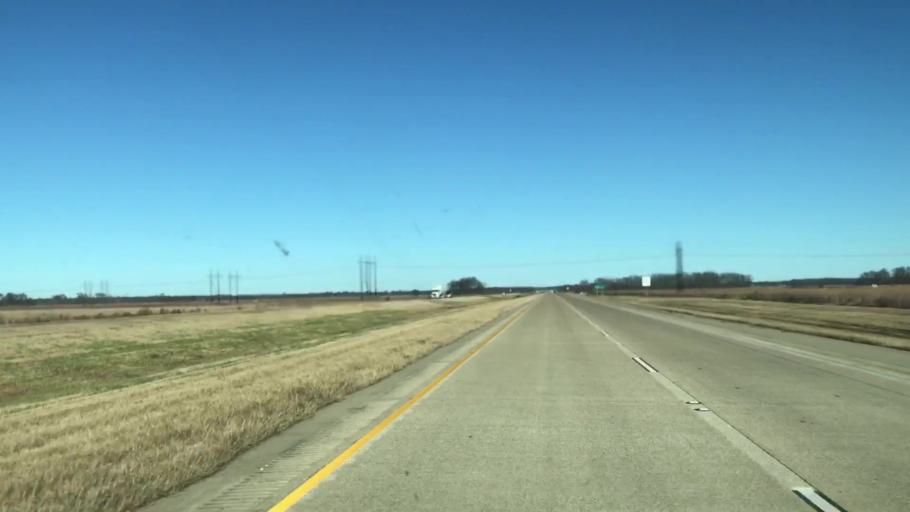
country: US
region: Louisiana
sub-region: Caddo Parish
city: Oil City
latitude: 32.7135
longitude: -93.8661
